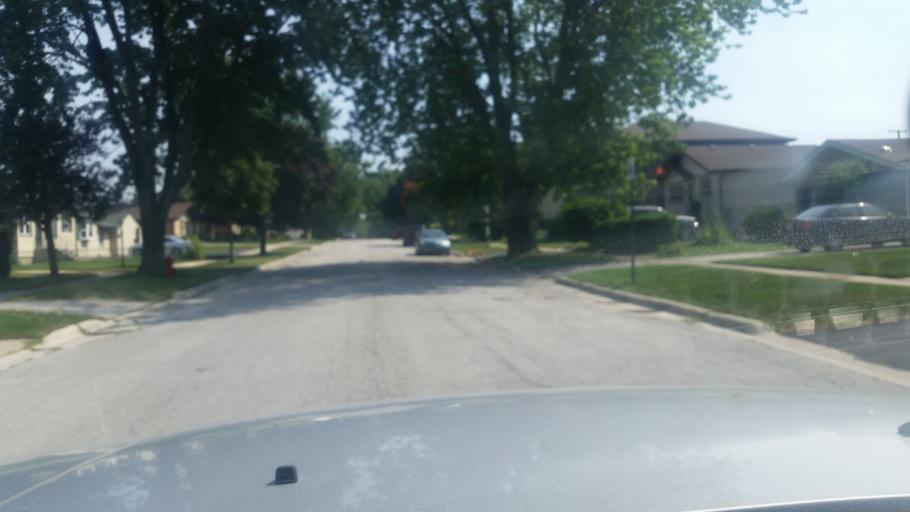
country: US
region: Illinois
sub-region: Cook County
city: Chicago Ridge
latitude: 41.6994
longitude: -87.7768
